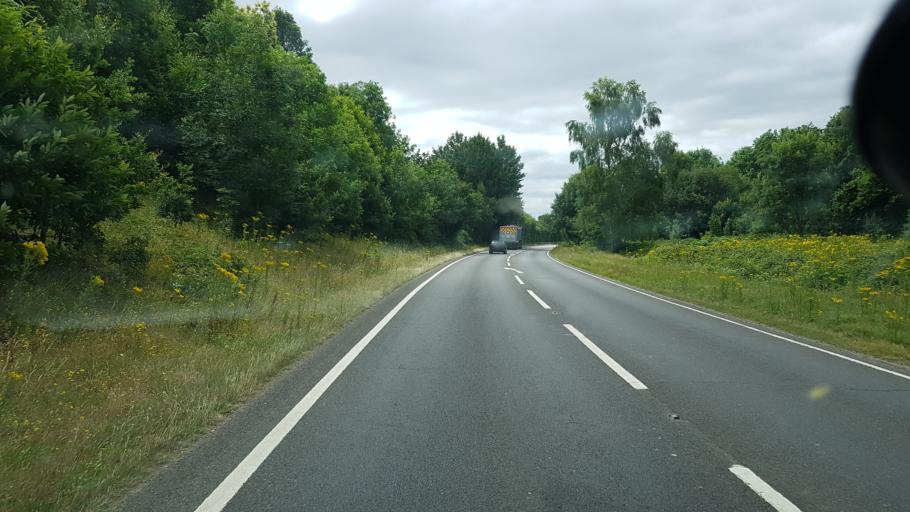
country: GB
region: England
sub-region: Surrey
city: Godstone
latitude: 51.2404
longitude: -0.0468
